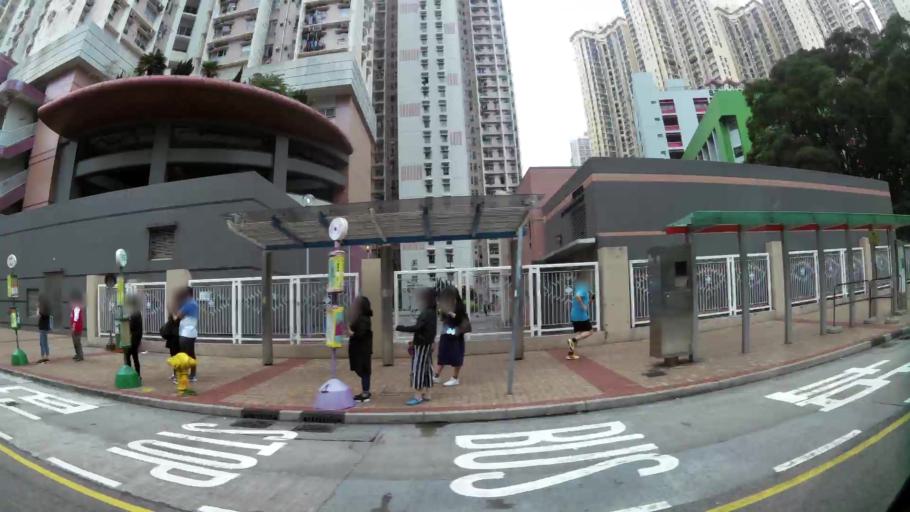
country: HK
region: Kowloon City
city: Kowloon
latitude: 22.3013
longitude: 114.2376
